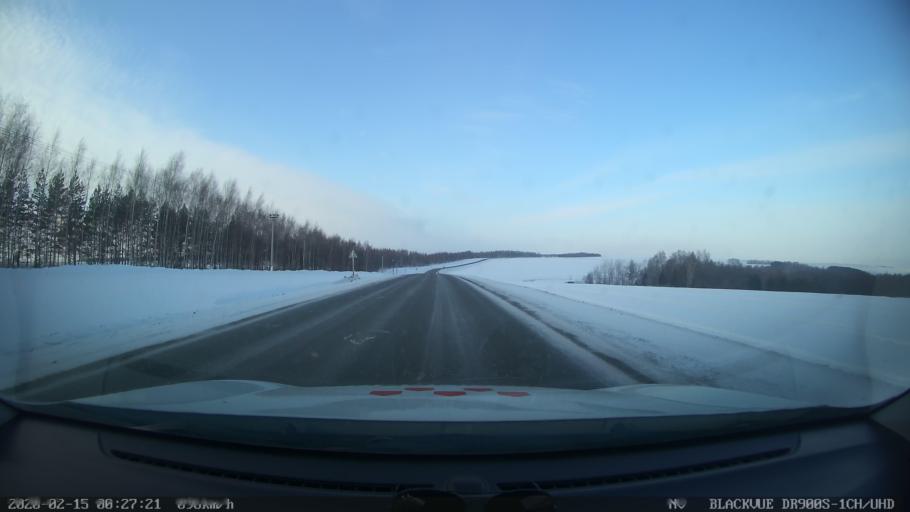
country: RU
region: Tatarstan
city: Verkhniy Uslon
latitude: 55.6270
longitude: 48.8752
